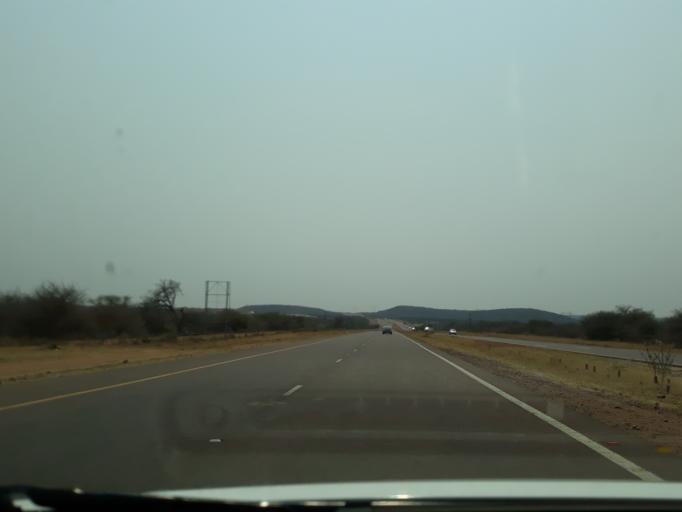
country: BW
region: Kgatleng
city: Bokaa
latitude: -24.4105
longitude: 26.0517
